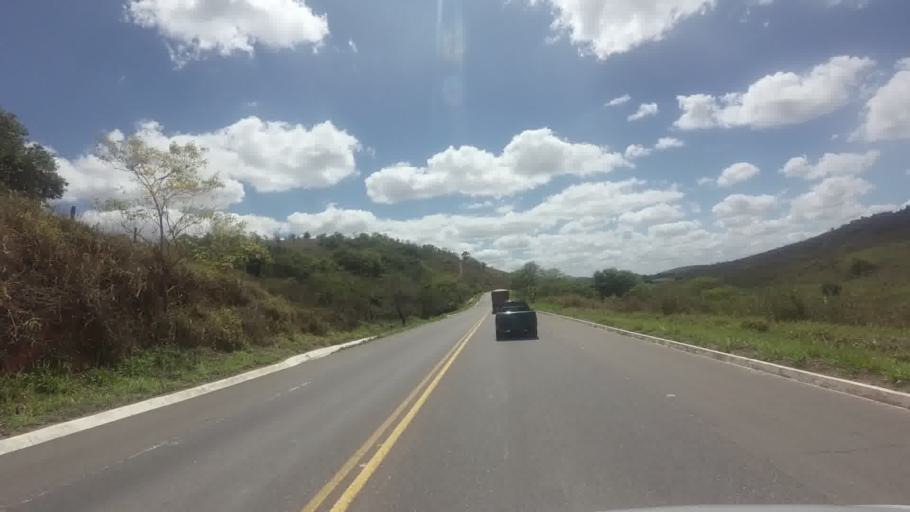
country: BR
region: Minas Gerais
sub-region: Recreio
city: Recreio
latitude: -21.6707
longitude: -42.3905
